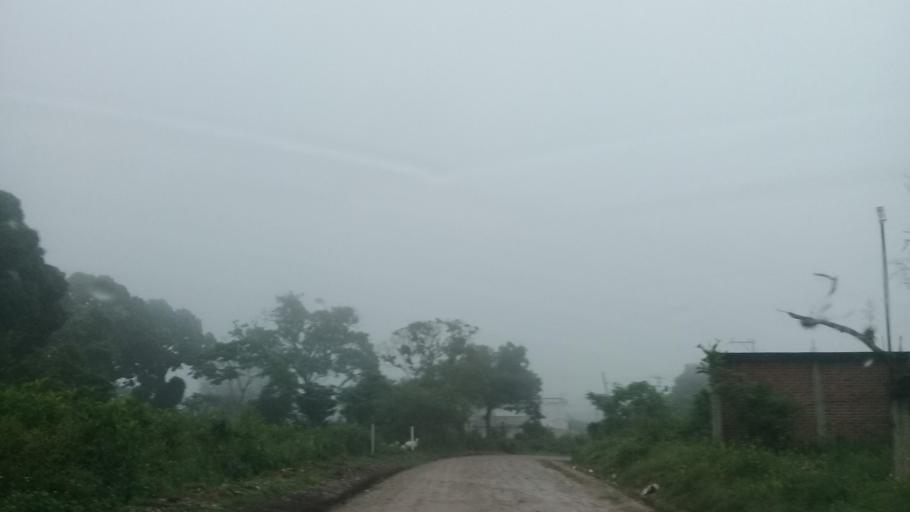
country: MX
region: Veracruz
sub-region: Xalapa
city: Fraccionamiento las Fuentes
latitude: 19.4931
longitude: -96.8817
